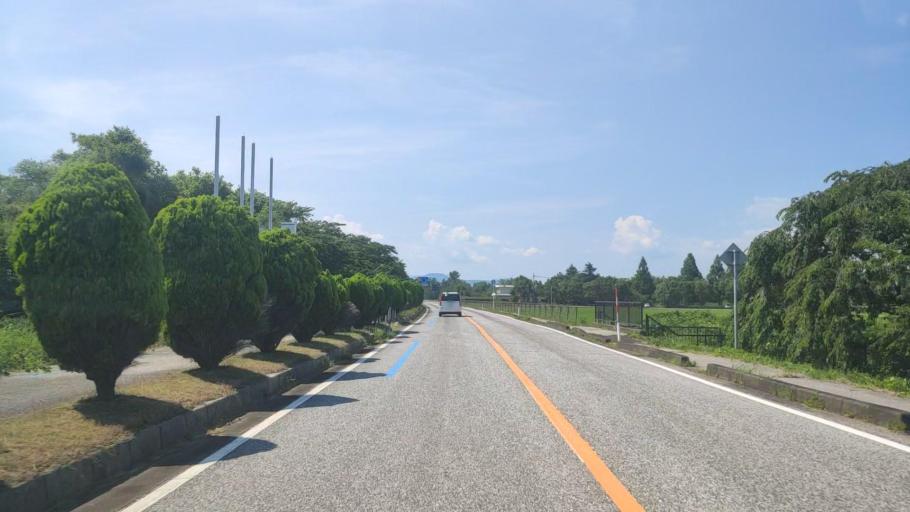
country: JP
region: Shiga Prefecture
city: Nagahama
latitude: 35.4072
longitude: 136.2127
